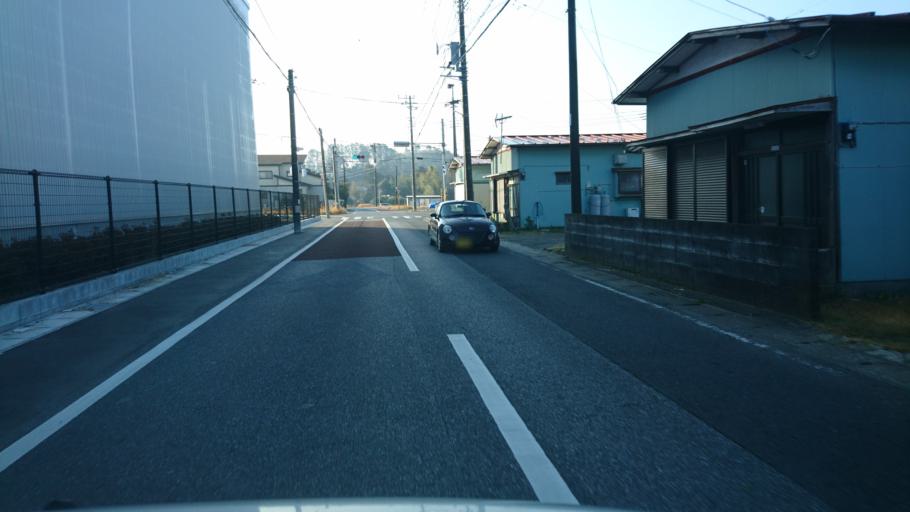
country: JP
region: Chiba
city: Kimitsu
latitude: 35.3047
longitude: 139.9473
